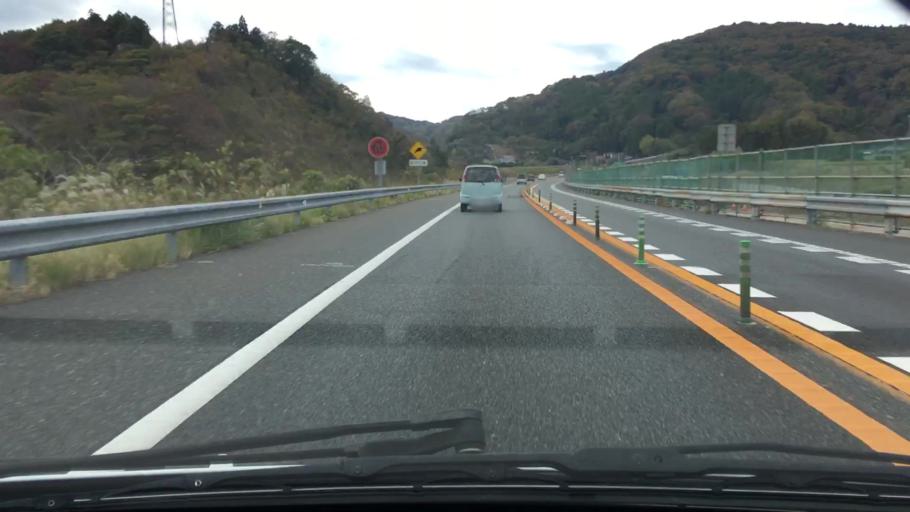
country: JP
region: Chiba
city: Futtsu
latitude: 35.2094
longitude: 139.8829
